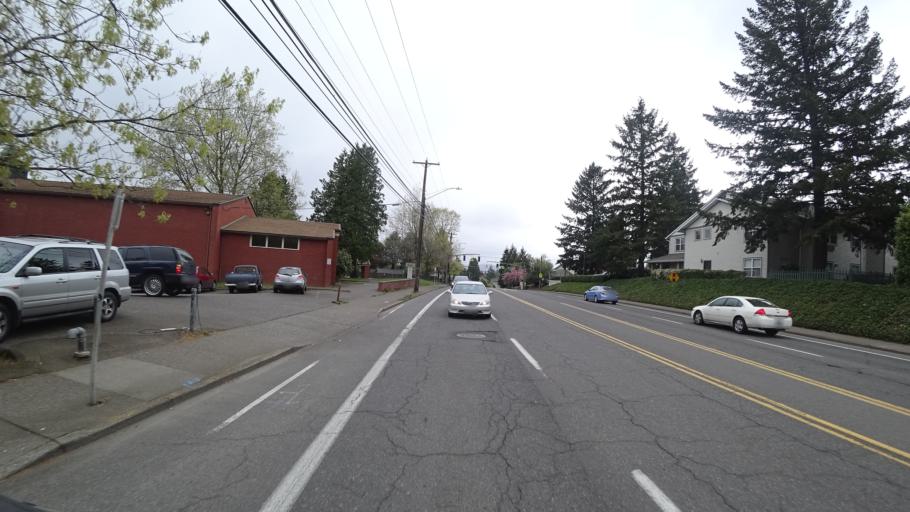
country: US
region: Oregon
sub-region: Washington County
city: Metzger
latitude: 45.4486
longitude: -122.7246
